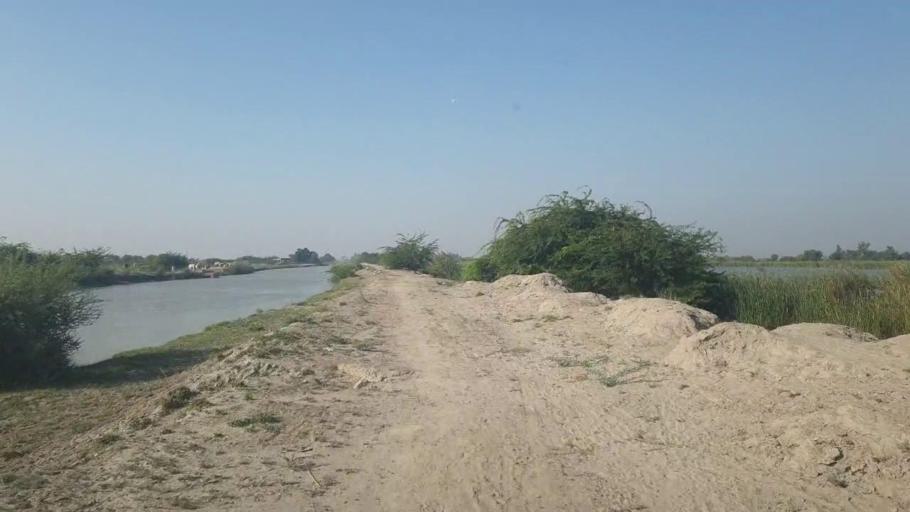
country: PK
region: Sindh
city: Badin
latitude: 24.7089
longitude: 68.8901
